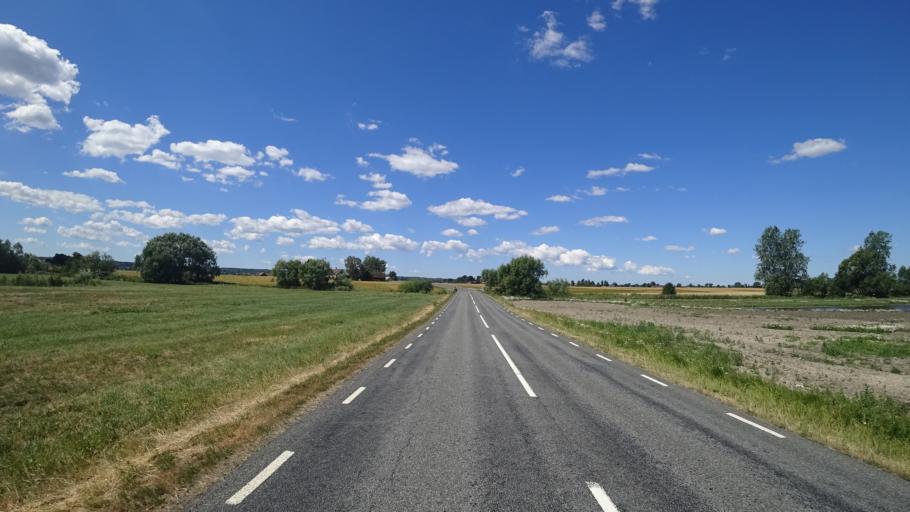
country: SE
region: Skane
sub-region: Kristianstads Kommun
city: Onnestad
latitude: 56.0657
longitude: 14.0521
